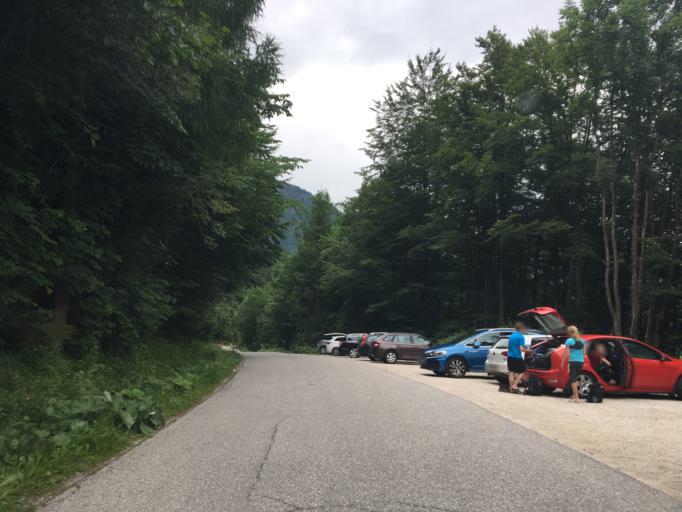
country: AT
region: Salzburg
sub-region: Politischer Bezirk Salzburg-Umgebung
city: Strobl
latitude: 47.6624
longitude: 13.4592
